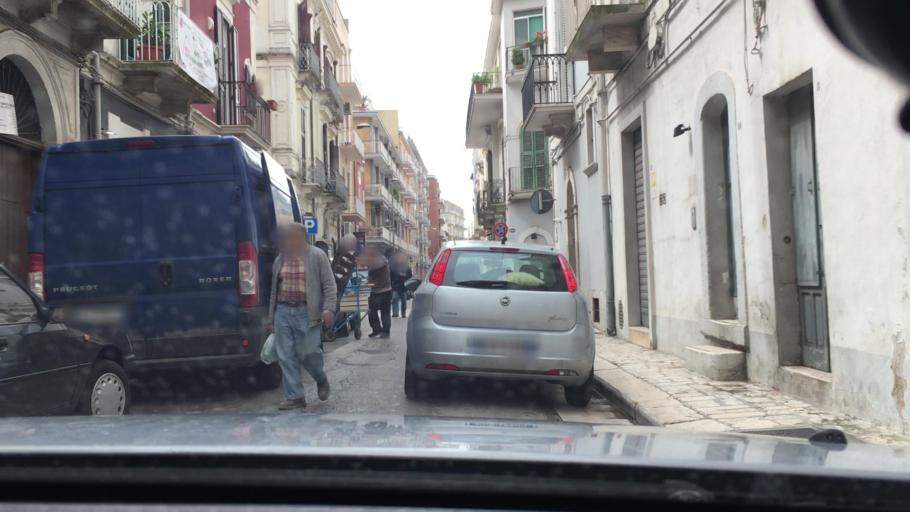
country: IT
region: Apulia
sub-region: Provincia di Bari
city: Gioia del Colle
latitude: 40.7977
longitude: 16.9207
